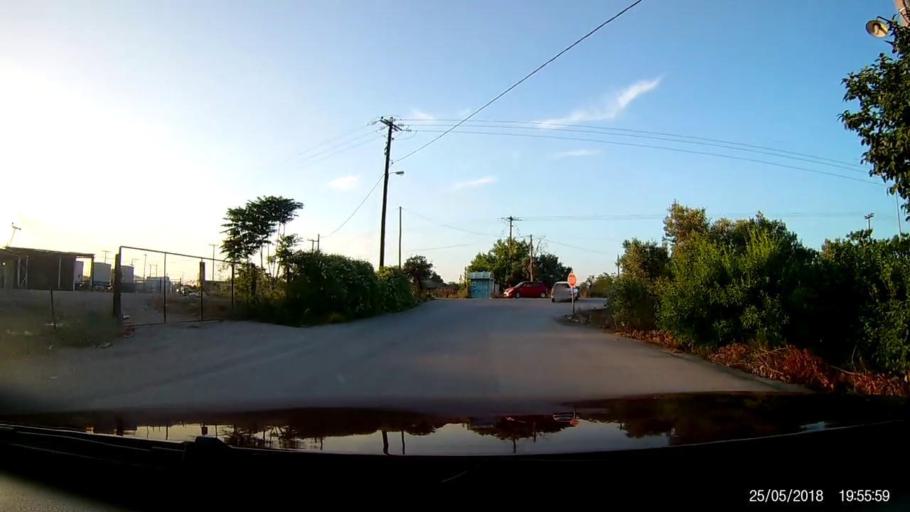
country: GR
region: Central Greece
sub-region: Nomos Evvoias
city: Vasilikon
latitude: 38.4284
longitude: 23.6606
